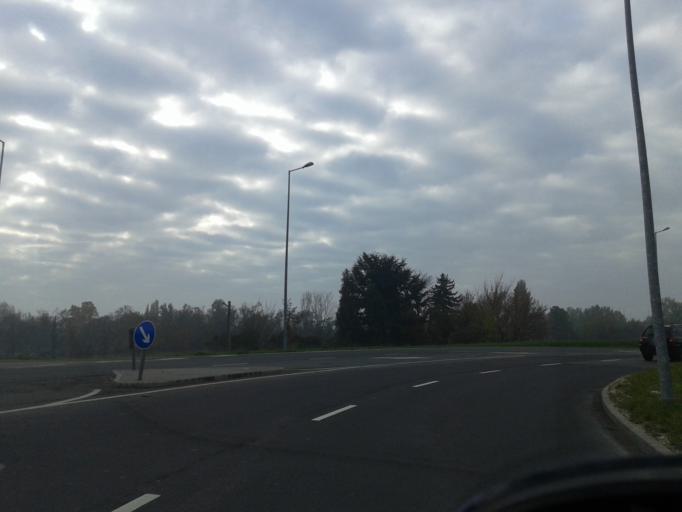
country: HU
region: Budapest
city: Budapest XXII. keruelet
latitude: 47.4009
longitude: 19.0157
